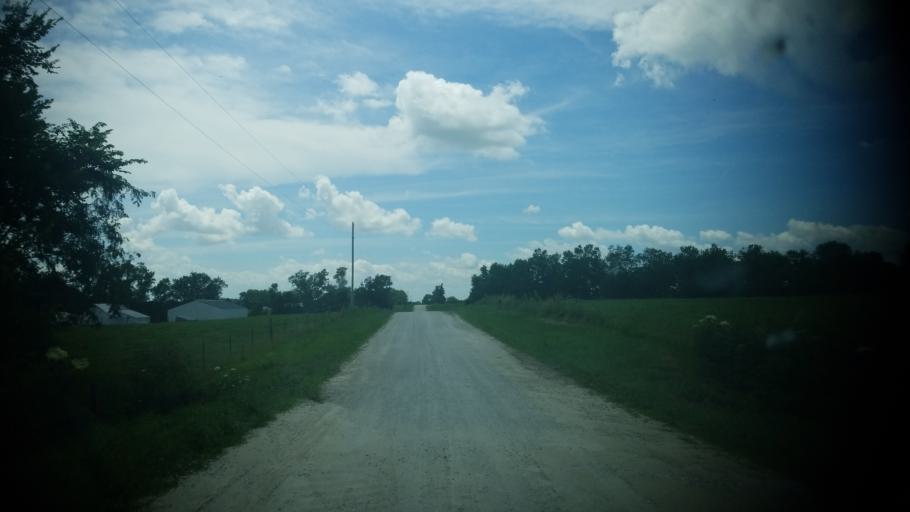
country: US
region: Missouri
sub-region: Pike County
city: Bowling Green
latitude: 39.3085
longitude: -91.3138
